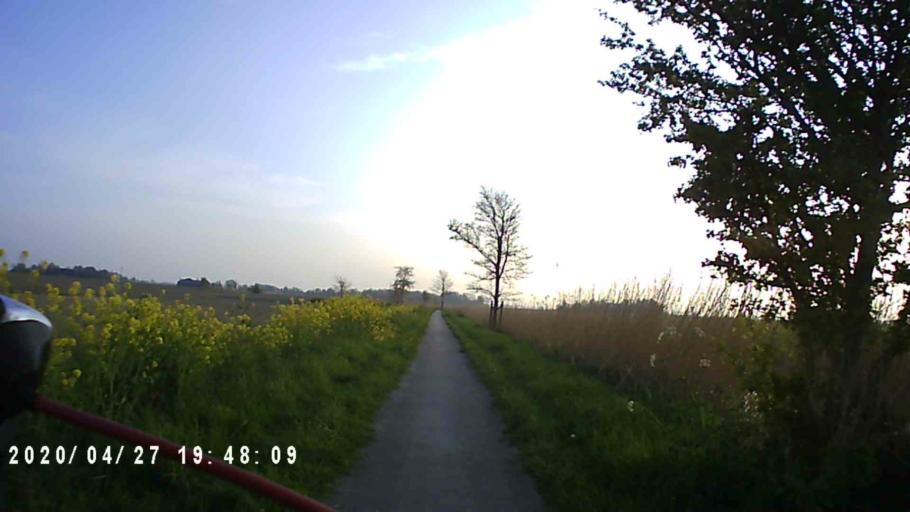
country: NL
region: Groningen
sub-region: Gemeente Zuidhorn
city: Oldehove
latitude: 53.3495
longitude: 6.4381
